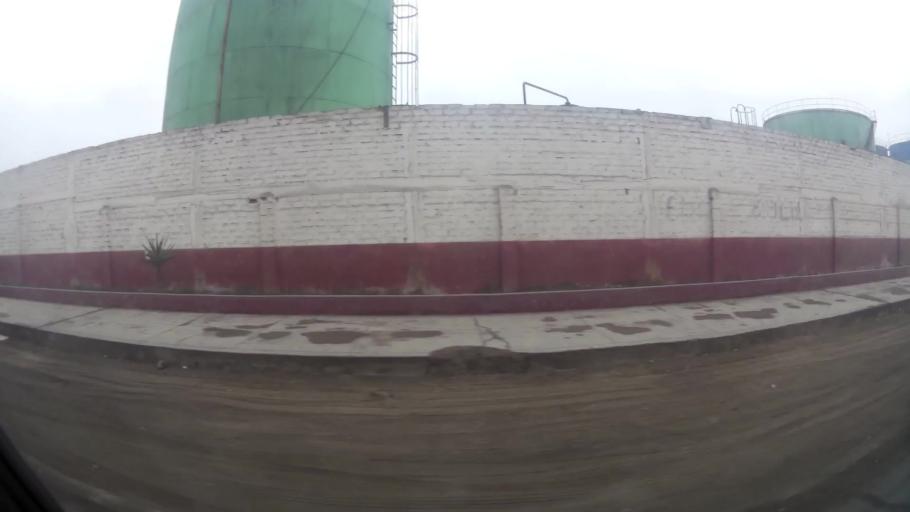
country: PE
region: Lima
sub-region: Provincia de Huaral
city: Chancay
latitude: -11.5765
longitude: -77.2694
